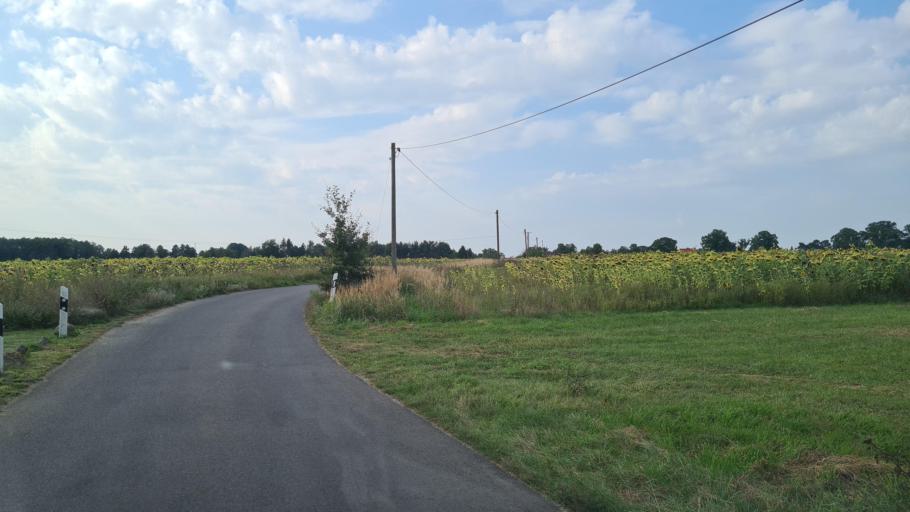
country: DE
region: Brandenburg
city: Drebkau
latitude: 51.6651
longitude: 14.2072
